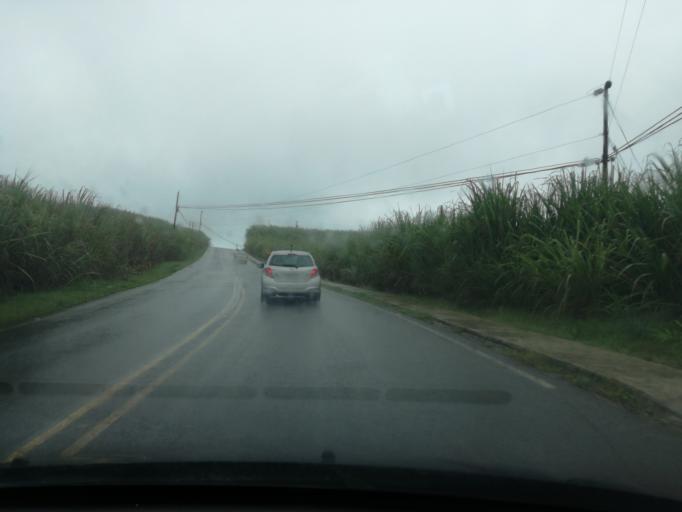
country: CR
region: Cartago
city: Tucurrique
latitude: 9.8930
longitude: -83.7609
